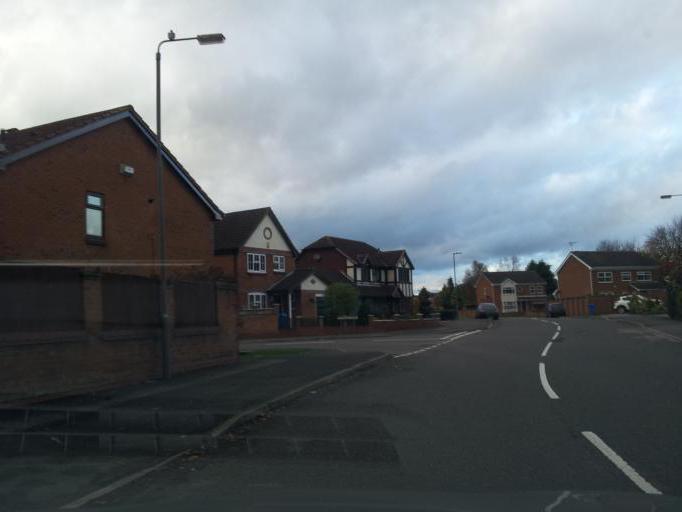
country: GB
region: England
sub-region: Derbyshire
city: Ilkeston
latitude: 52.9855
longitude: -1.3226
